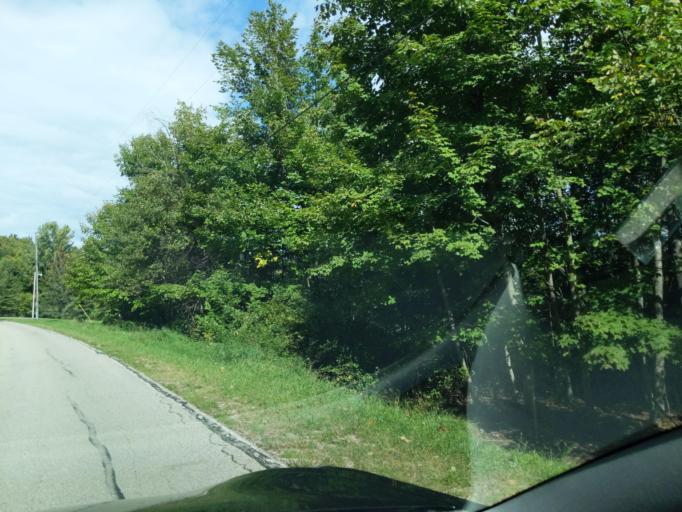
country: US
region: Michigan
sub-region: Antrim County
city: Elk Rapids
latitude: 44.9574
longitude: -85.3235
